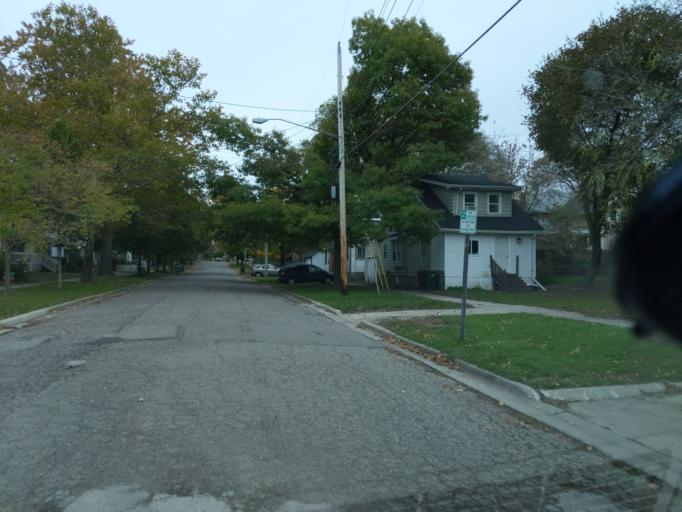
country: US
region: Michigan
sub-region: Ingham County
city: Lansing
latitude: 42.7399
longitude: -84.5643
